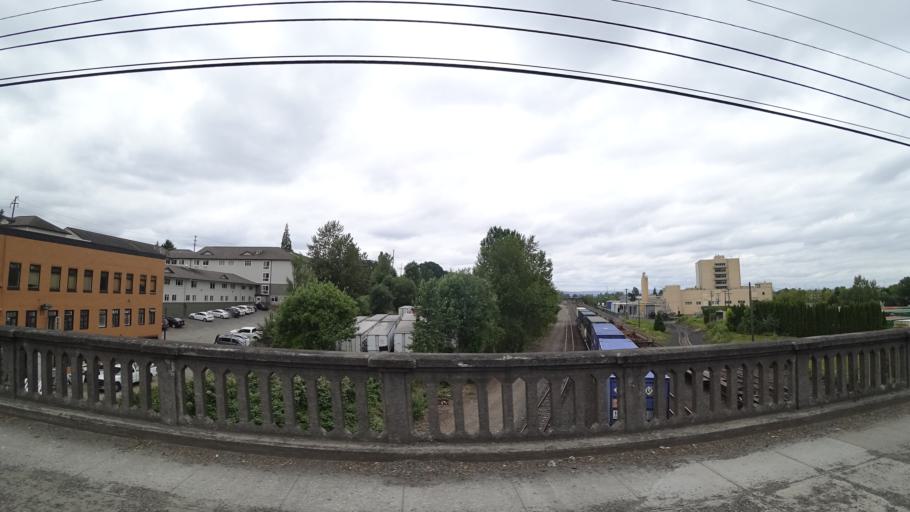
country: US
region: Oregon
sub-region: Multnomah County
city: Portland
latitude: 45.5788
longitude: -122.6614
